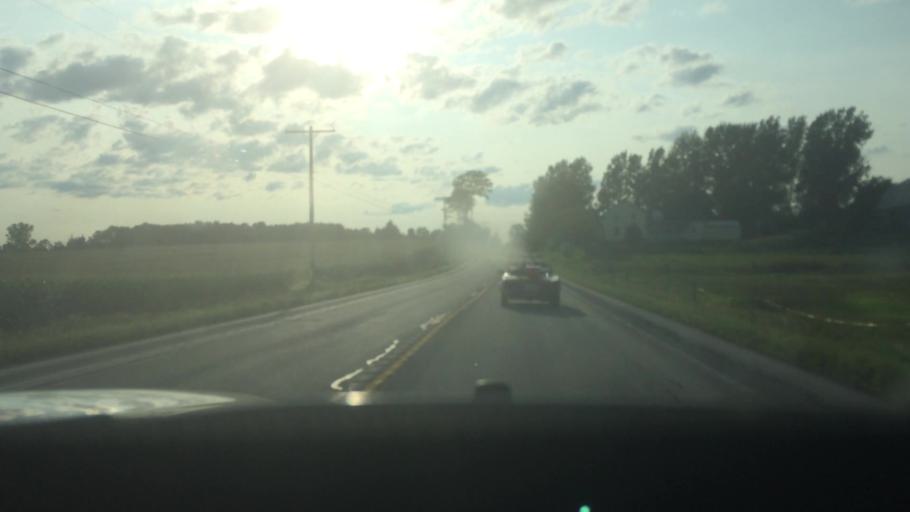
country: US
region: New York
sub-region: St. Lawrence County
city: Ogdensburg
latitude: 44.6646
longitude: -75.3511
